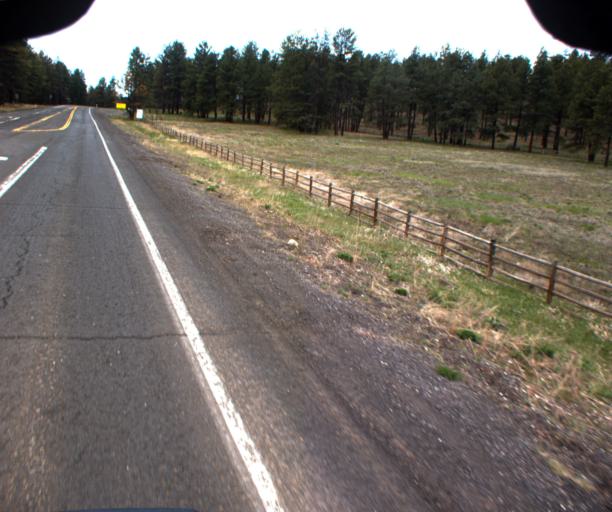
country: US
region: Arizona
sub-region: Coconino County
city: Kachina Village
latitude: 35.1281
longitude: -111.6914
